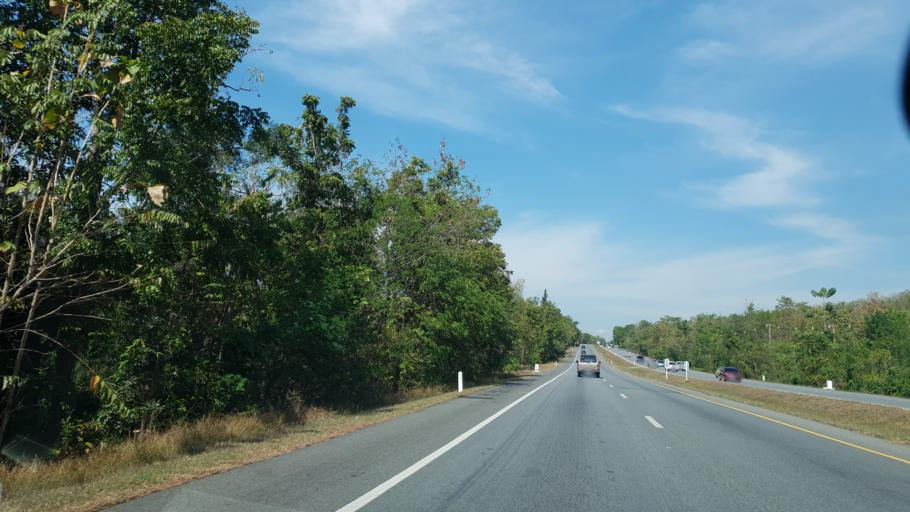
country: TH
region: Uttaradit
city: Thong Saen Khan
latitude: 17.4164
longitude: 100.2274
